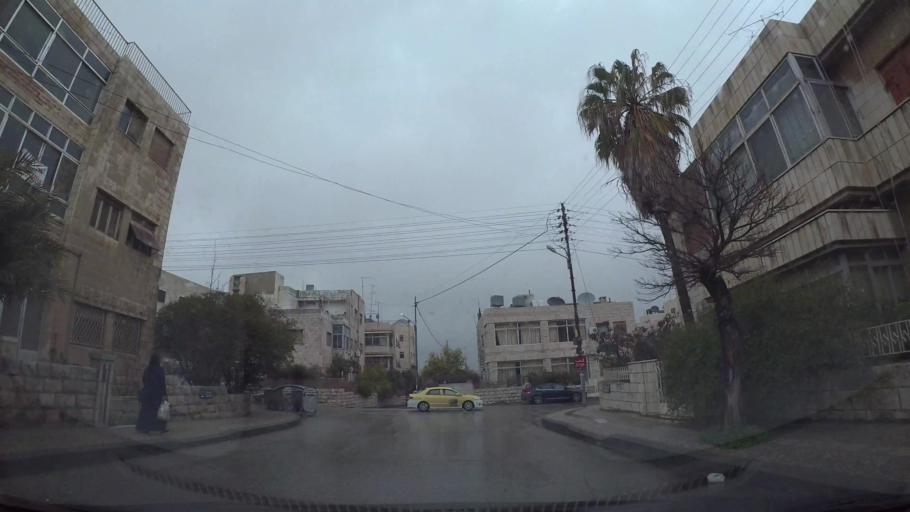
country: JO
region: Amman
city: Amman
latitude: 31.9721
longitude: 35.9174
